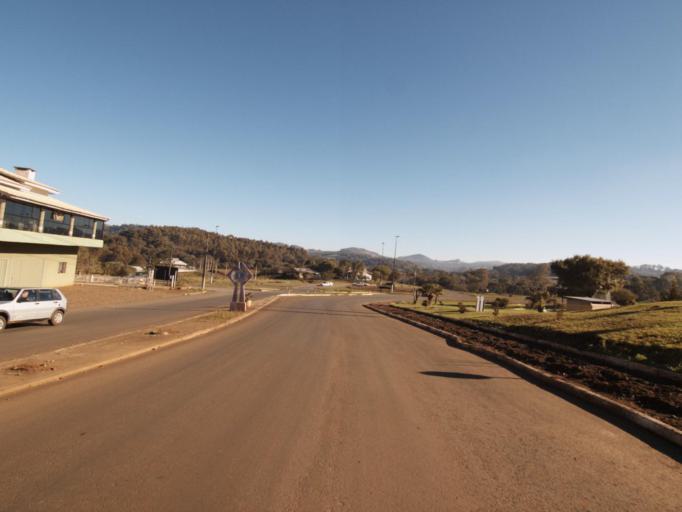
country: BR
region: Rio Grande do Sul
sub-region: Frederico Westphalen
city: Frederico Westphalen
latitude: -26.8888
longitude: -53.1767
